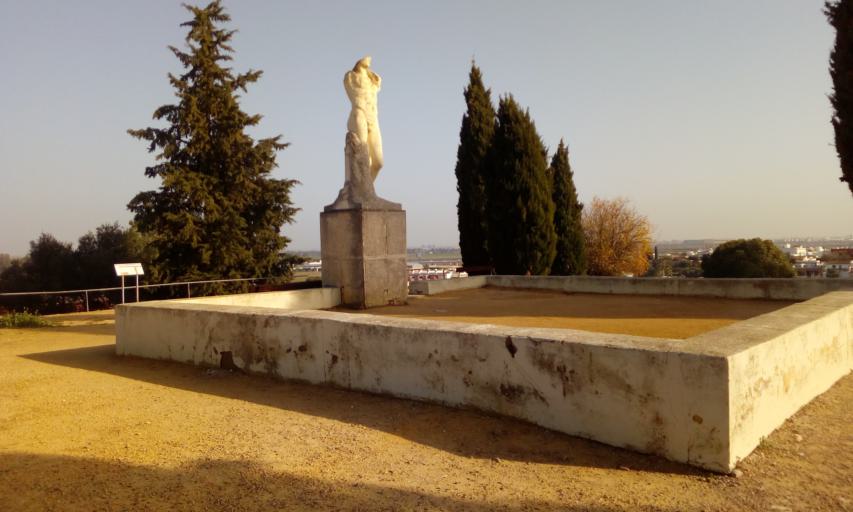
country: ES
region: Andalusia
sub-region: Provincia de Sevilla
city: Santiponce
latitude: 37.4423
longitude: -6.0437
